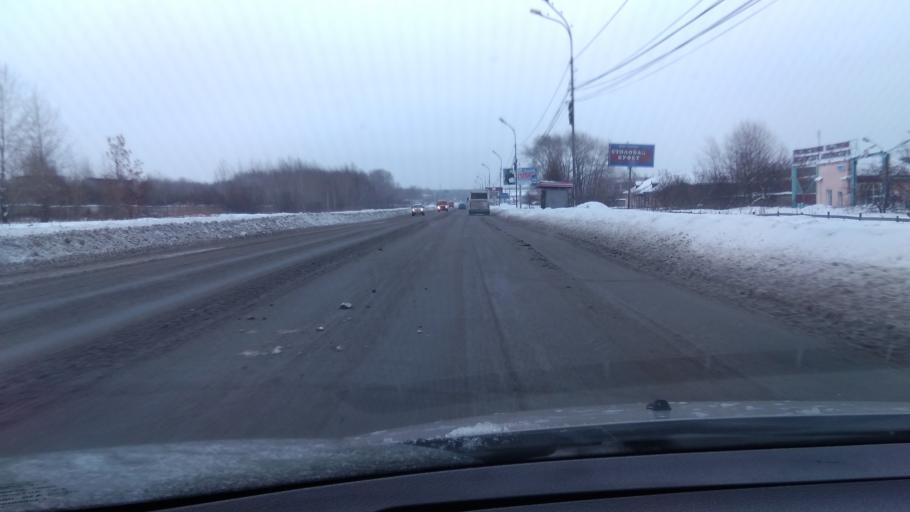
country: RU
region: Sverdlovsk
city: Nizhniy Tagil
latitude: 57.9090
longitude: 60.0166
